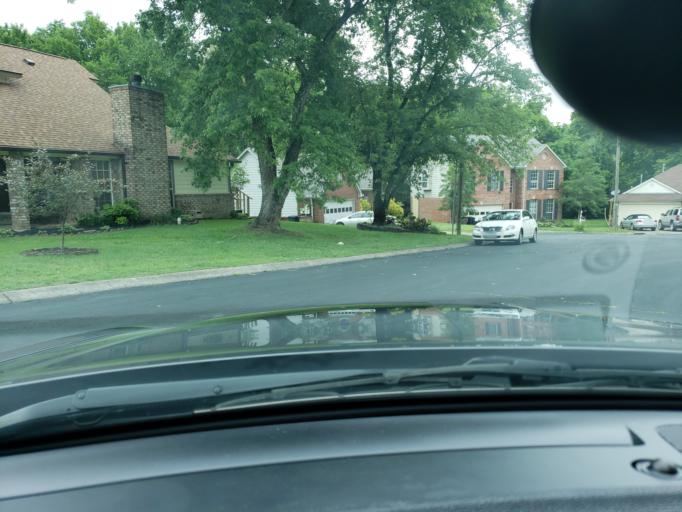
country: US
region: Tennessee
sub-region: Williamson County
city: Nolensville
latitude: 36.0351
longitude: -86.6770
